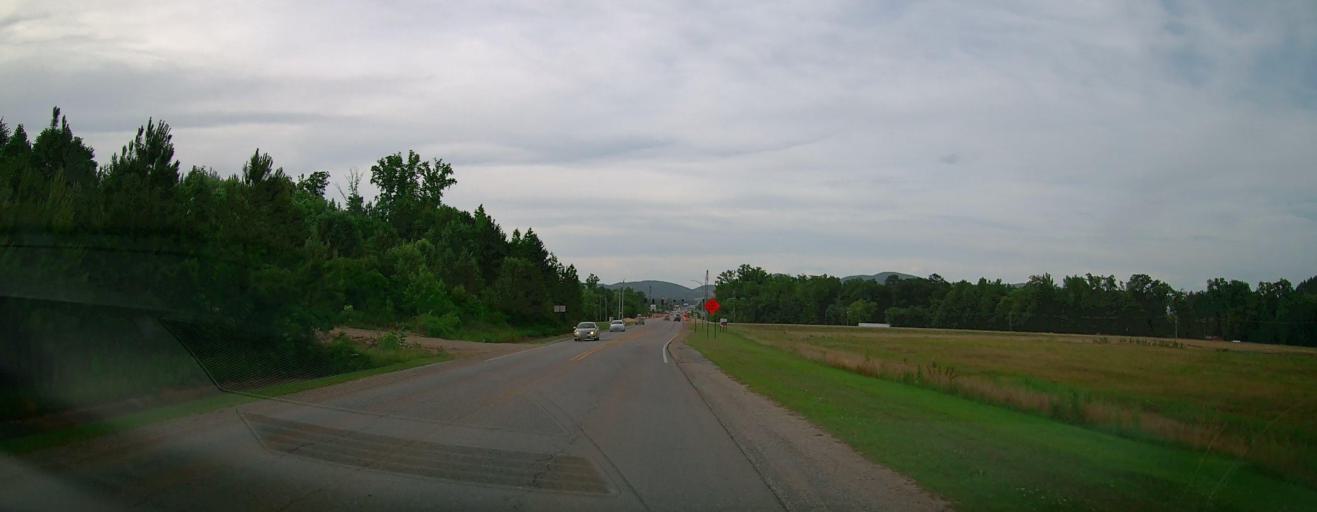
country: US
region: Alabama
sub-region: Calhoun County
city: Oxford
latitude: 33.5984
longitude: -85.7860
